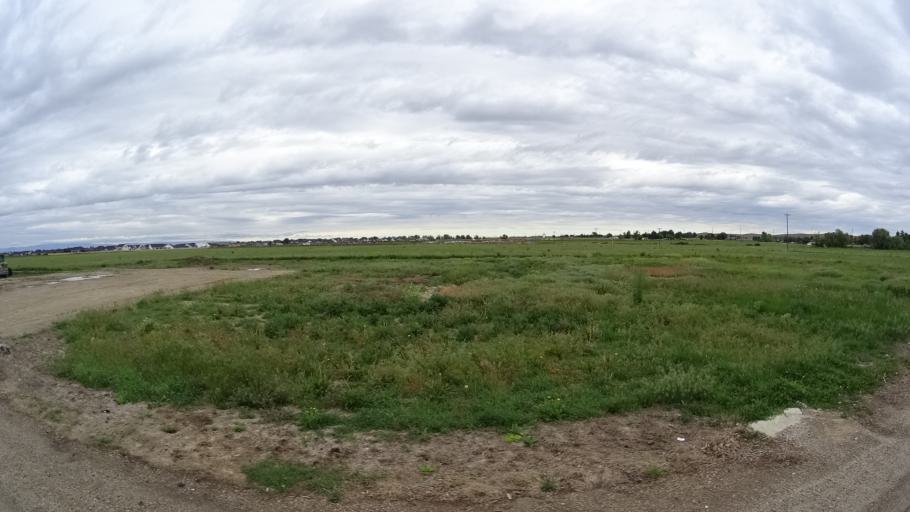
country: US
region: Idaho
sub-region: Ada County
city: Eagle
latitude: 43.7163
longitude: -116.4135
